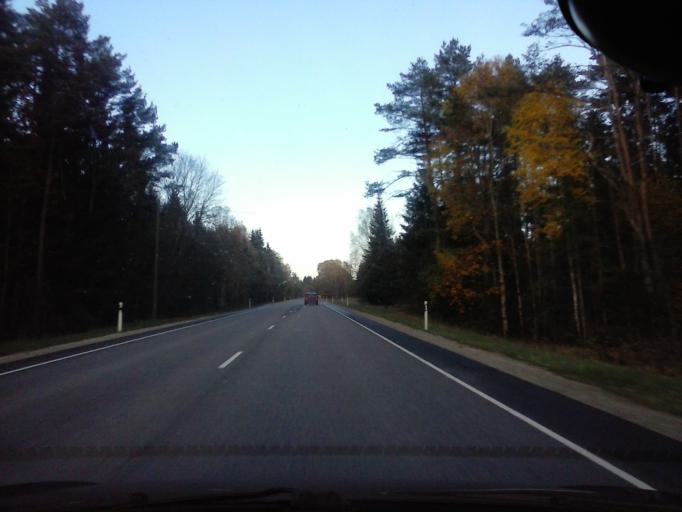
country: EE
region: Harju
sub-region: Nissi vald
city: Turba
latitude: 58.9882
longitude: 24.0169
